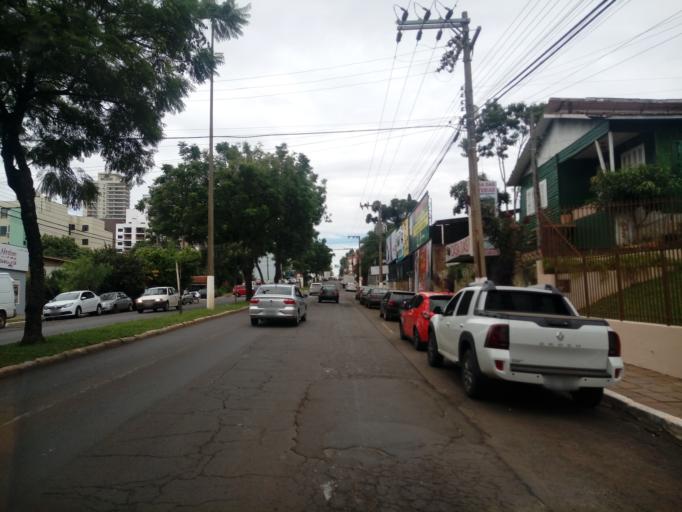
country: BR
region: Santa Catarina
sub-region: Chapeco
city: Chapeco
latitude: -27.1070
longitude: -52.6189
